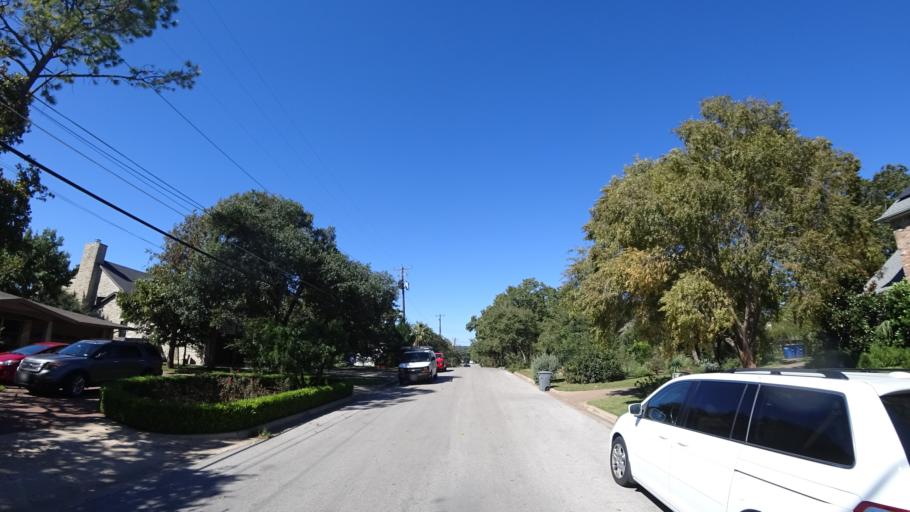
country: US
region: Texas
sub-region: Travis County
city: Rollingwood
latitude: 30.2995
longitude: -97.7641
